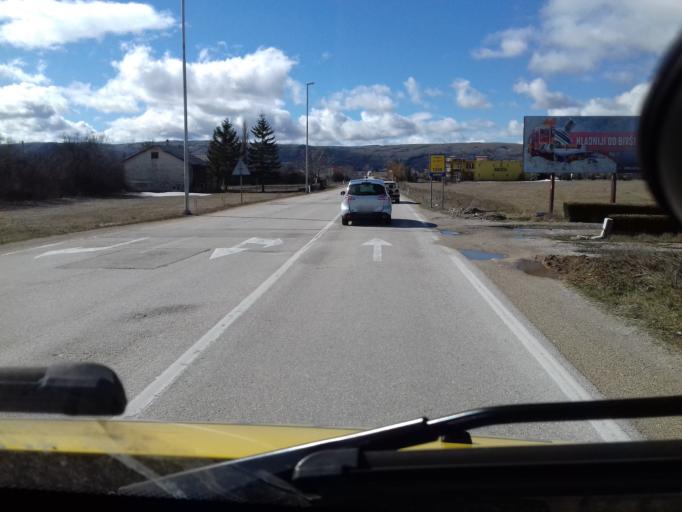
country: BA
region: Federation of Bosnia and Herzegovina
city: Tomislavgrad
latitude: 43.7000
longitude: 17.2156
